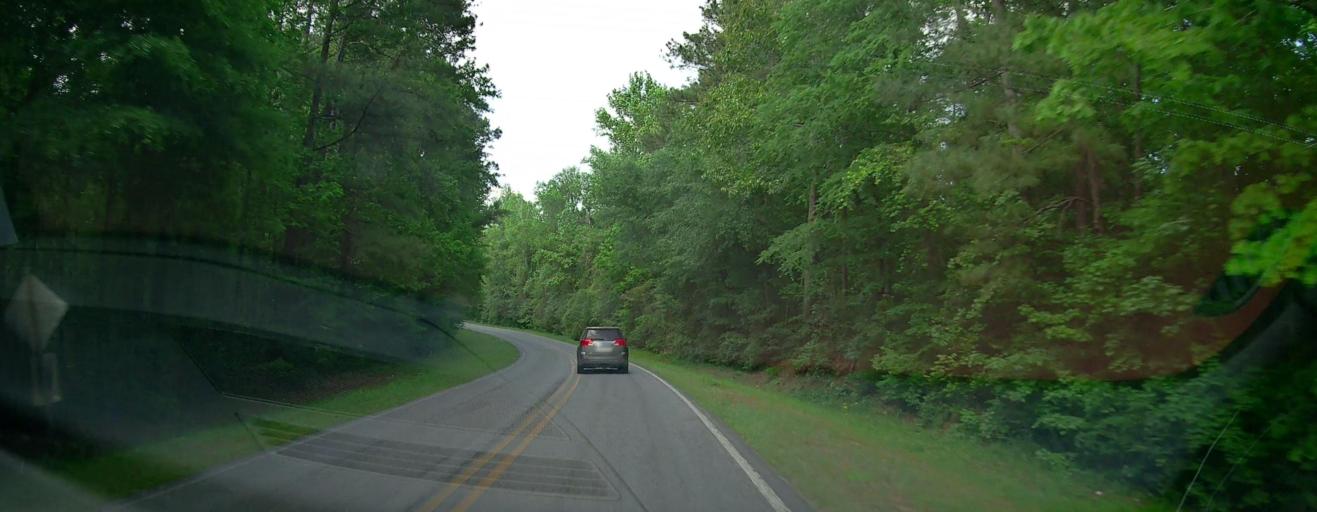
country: US
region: Georgia
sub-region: Laurens County
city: East Dublin
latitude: 32.6653
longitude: -82.8947
